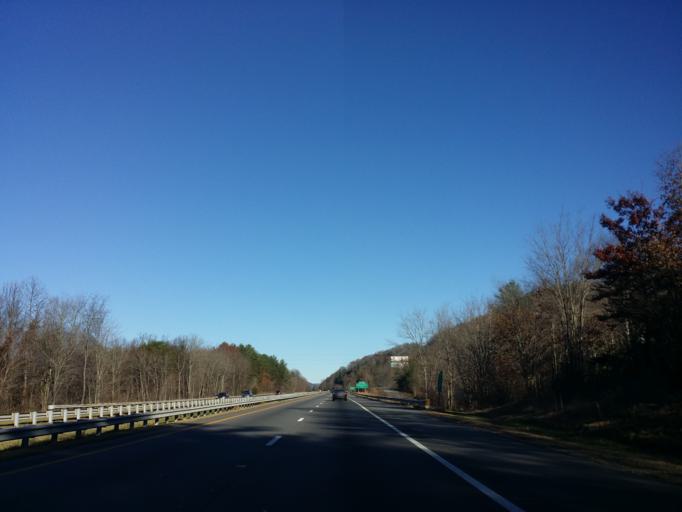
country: US
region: North Carolina
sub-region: Buncombe County
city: Swannanoa
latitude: 35.5917
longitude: -82.4279
